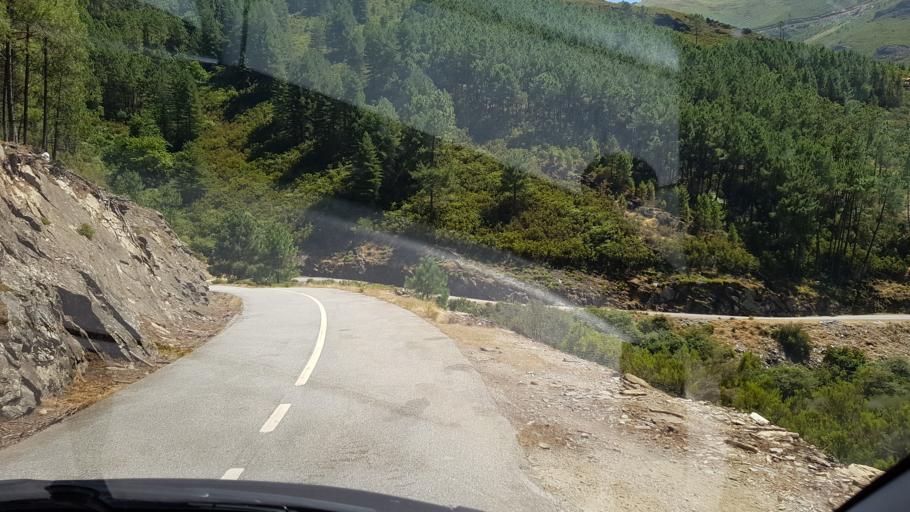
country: PT
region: Vila Real
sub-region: Mondim de Basto
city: Mondim de Basto
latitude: 41.3341
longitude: -7.8816
